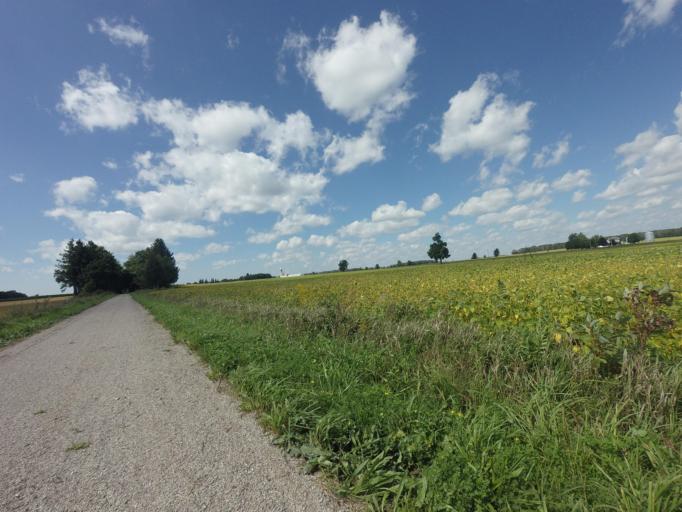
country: CA
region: Ontario
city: Huron East
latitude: 43.6665
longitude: -81.2661
